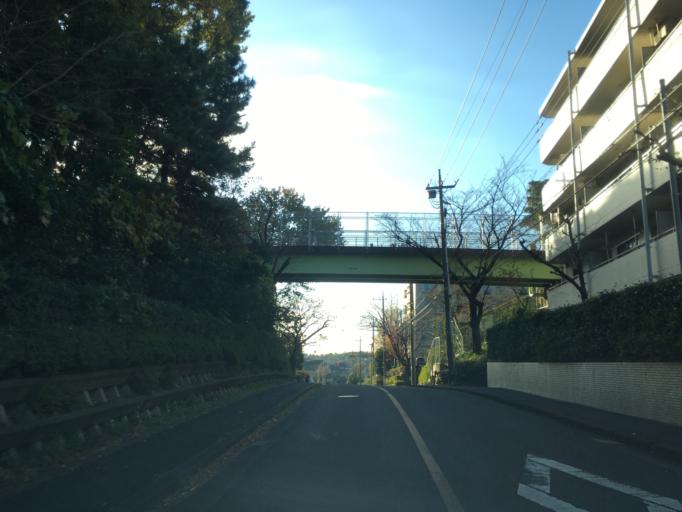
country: JP
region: Saitama
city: Tokorozawa
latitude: 35.7816
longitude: 139.4333
